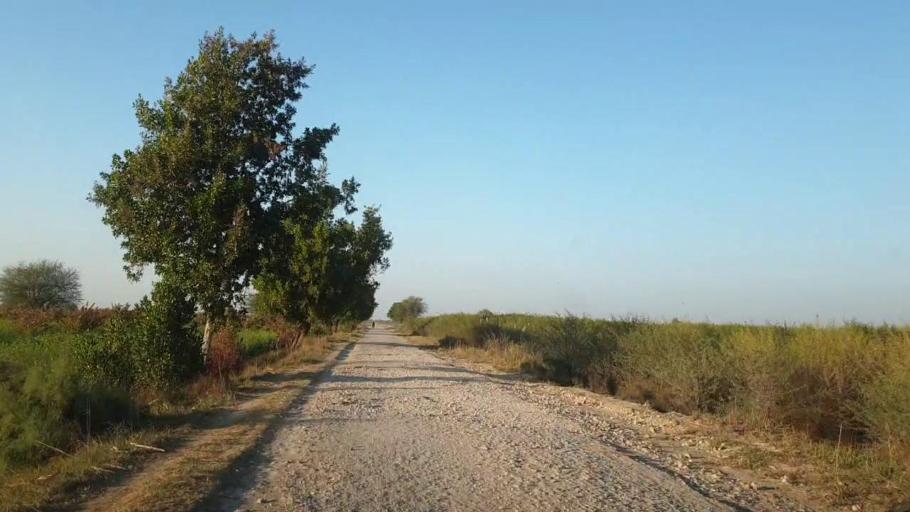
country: PK
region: Sindh
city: Mirpur Khas
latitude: 25.6699
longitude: 69.0480
